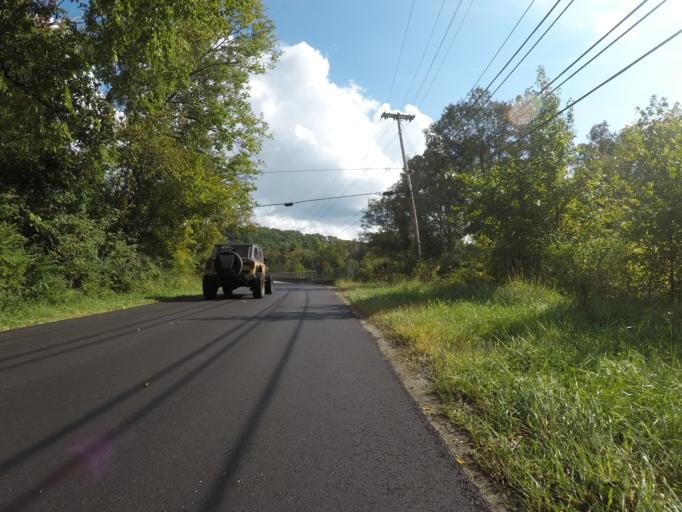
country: US
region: West Virginia
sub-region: Cabell County
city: Huntington
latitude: 38.3921
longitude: -82.4294
